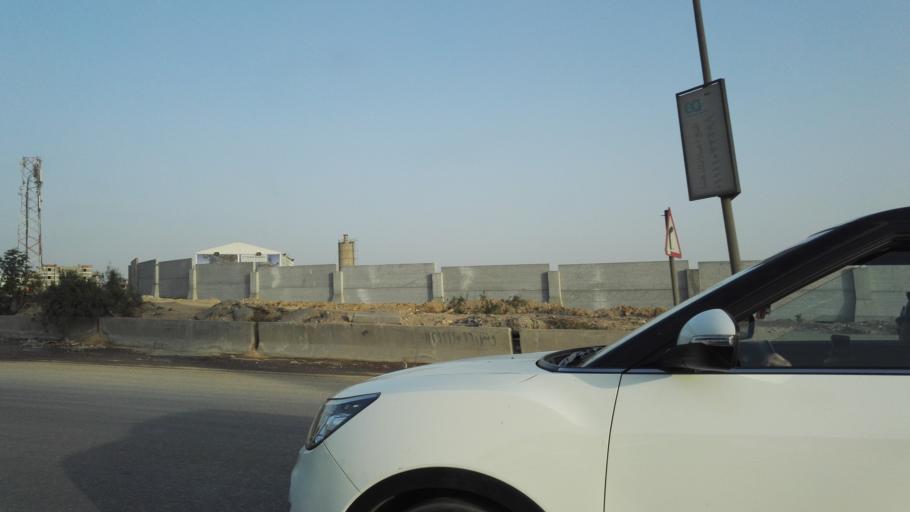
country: EG
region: Muhafazat al Qahirah
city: Cairo
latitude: 29.9918
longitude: 31.3806
